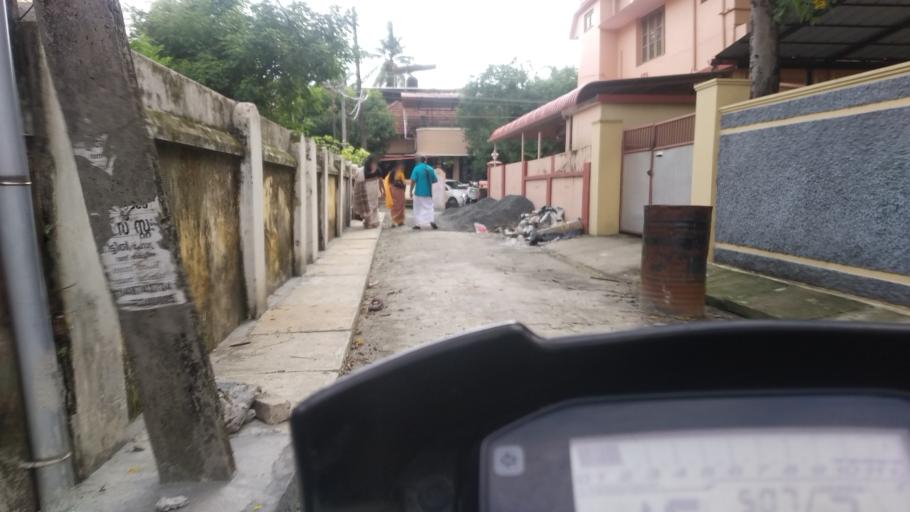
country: IN
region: Kerala
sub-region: Ernakulam
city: Cochin
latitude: 9.9944
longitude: 76.2802
